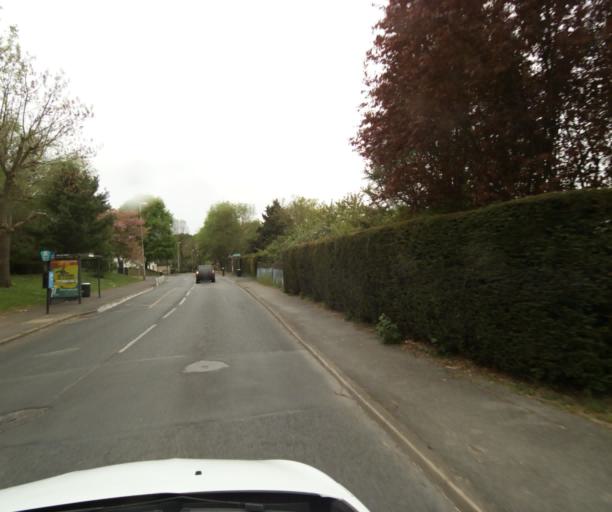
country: FR
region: Ile-de-France
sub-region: Departement de Seine-et-Marne
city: Torcy
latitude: 48.8547
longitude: 2.6378
